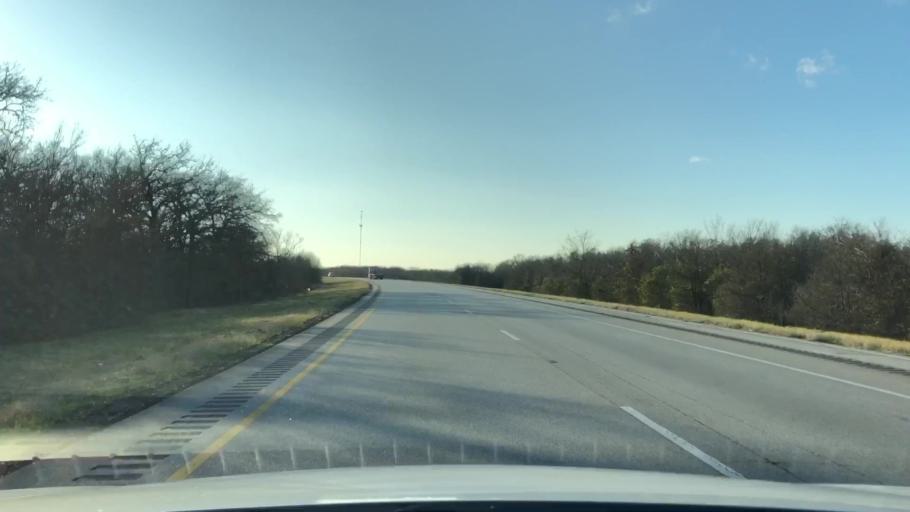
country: US
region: Texas
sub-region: Fayette County
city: Flatonia
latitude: 29.6967
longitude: -97.1424
